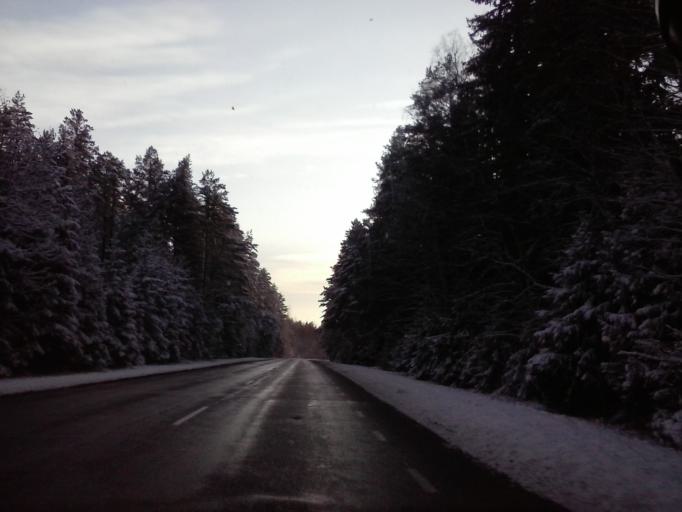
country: EE
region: Tartu
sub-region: UElenurme vald
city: Ulenurme
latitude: 58.3352
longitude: 26.8948
